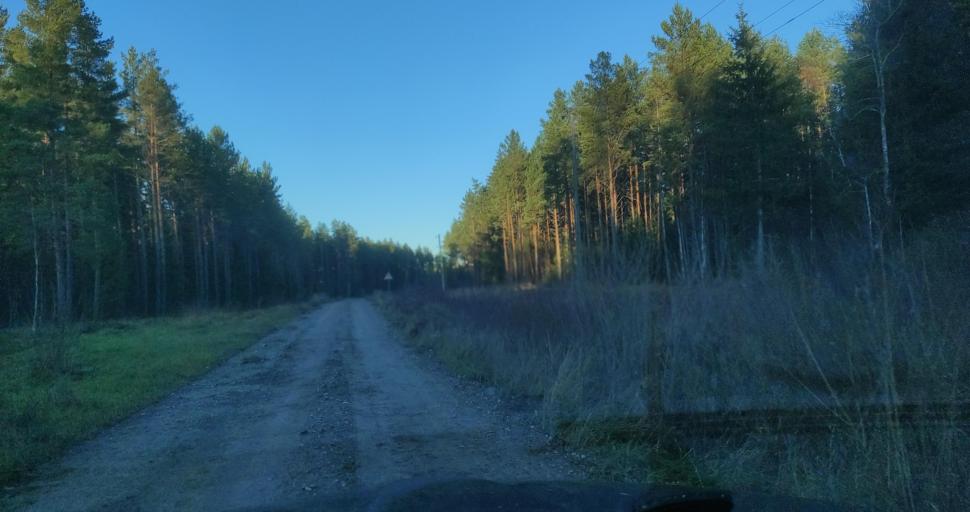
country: LV
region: Dundaga
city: Dundaga
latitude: 57.3742
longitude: 22.0786
